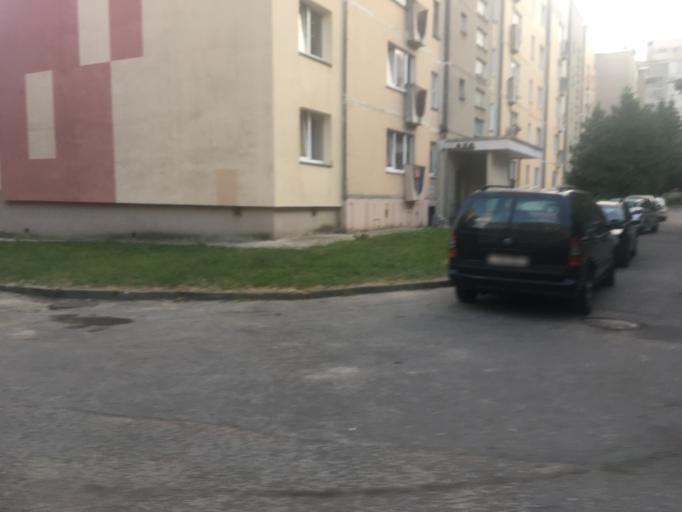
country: BY
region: Grodnenskaya
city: Hrodna
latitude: 53.6951
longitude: 23.8087
